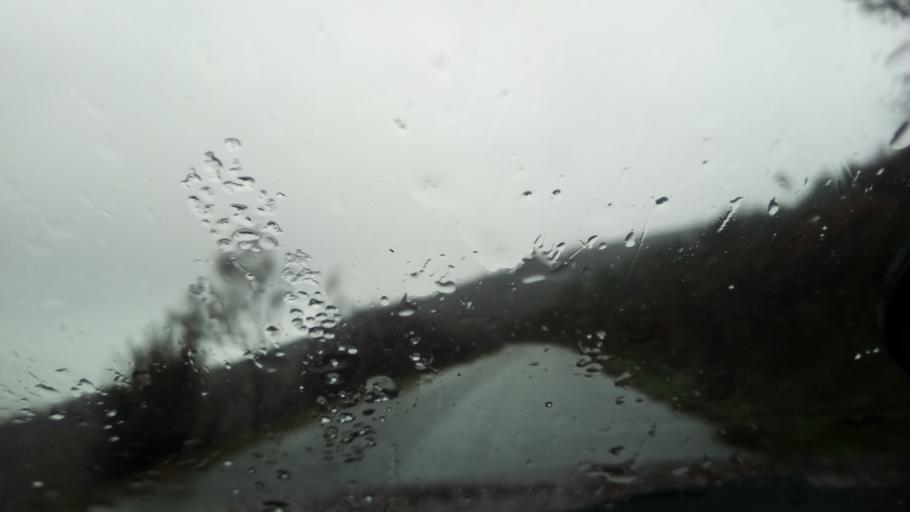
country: PT
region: Guarda
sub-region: Celorico da Beira
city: Celorico da Beira
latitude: 40.5371
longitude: -7.4452
